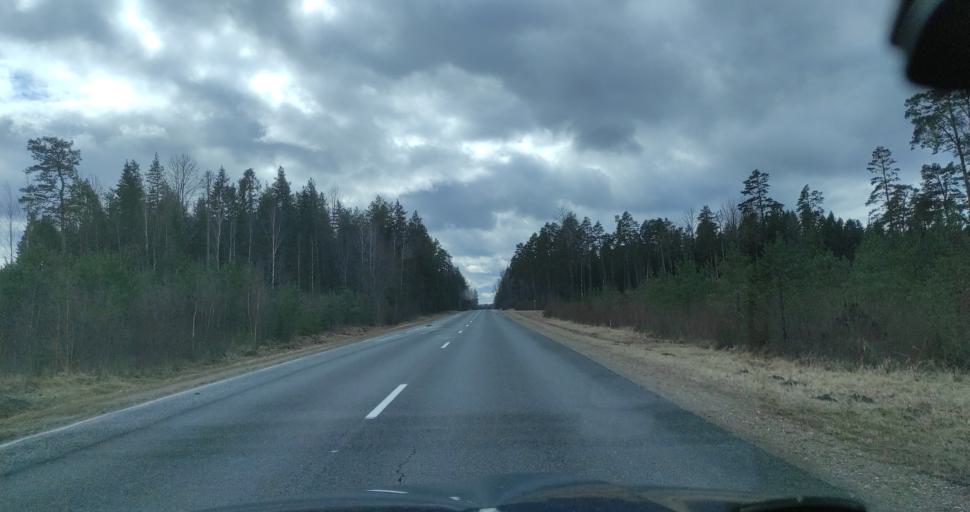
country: LV
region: Talsu Rajons
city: Stende
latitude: 57.0965
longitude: 22.4813
